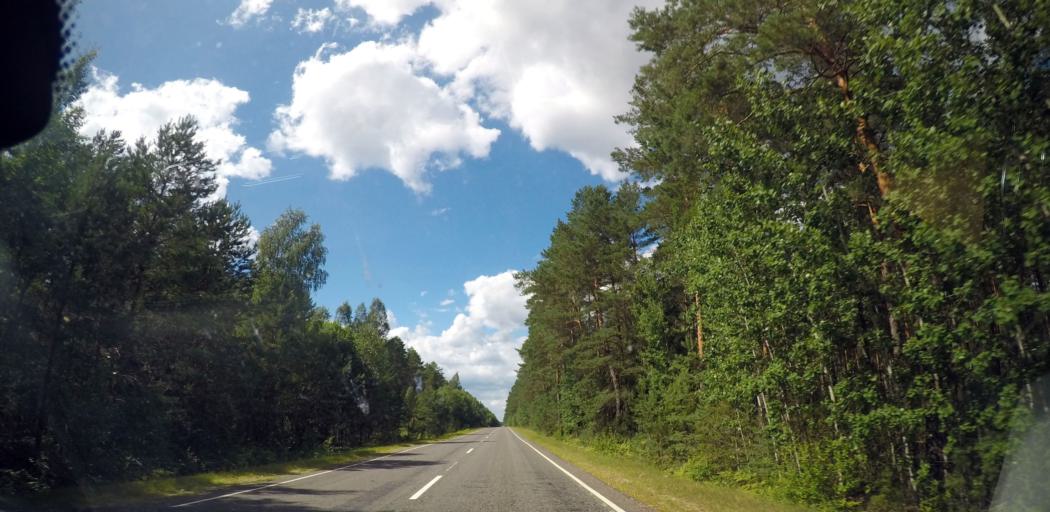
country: BY
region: Grodnenskaya
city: Skidal'
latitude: 53.8529
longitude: 24.1918
